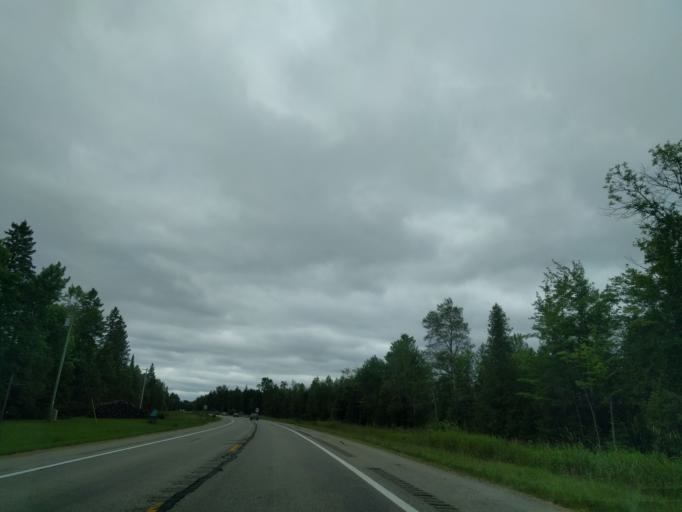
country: US
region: Michigan
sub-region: Delta County
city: Escanaba
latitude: 45.6619
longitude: -87.1736
